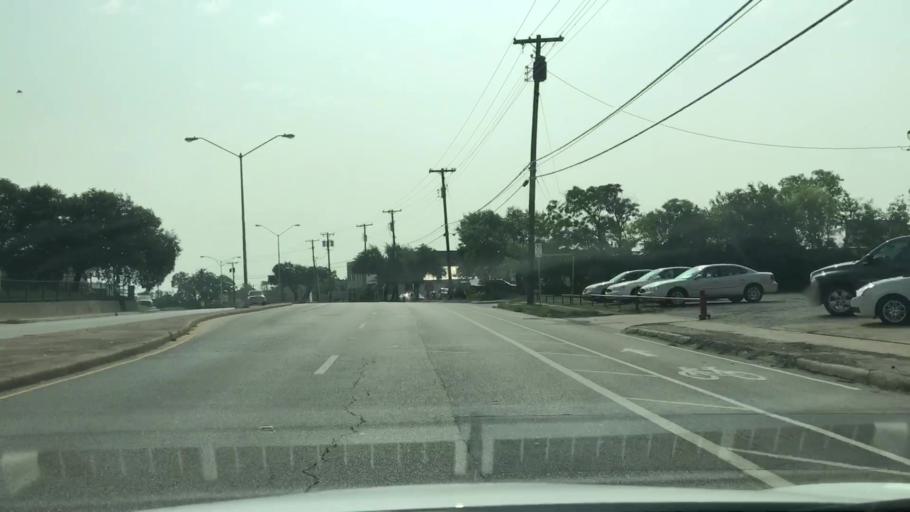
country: US
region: Texas
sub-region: Dallas County
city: Dallas
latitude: 32.7654
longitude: -96.8465
